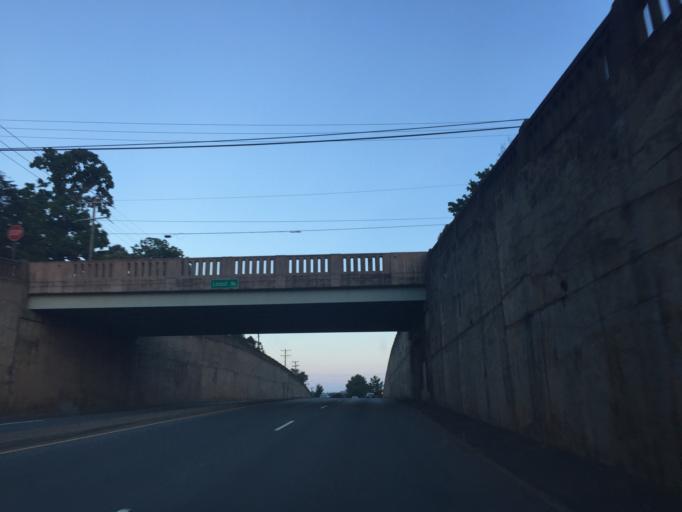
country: US
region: Virginia
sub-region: City of Charlottesville
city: Charlottesville
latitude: 38.0385
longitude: -78.4663
